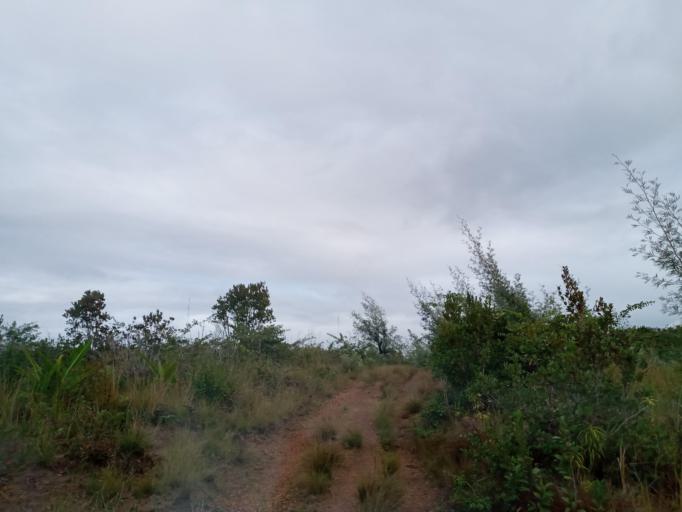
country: MG
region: Atsimo-Atsinanana
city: Vohipaho
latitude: -24.0048
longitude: 47.4088
